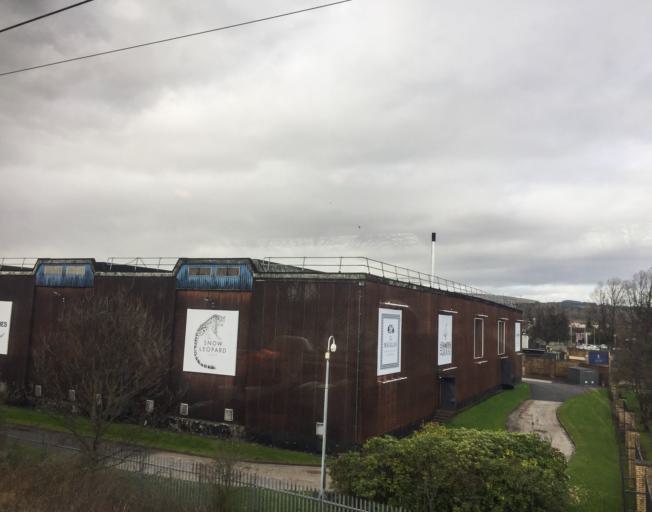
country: GB
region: Scotland
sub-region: West Dunbartonshire
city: Clydebank
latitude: 55.9055
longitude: -4.3706
